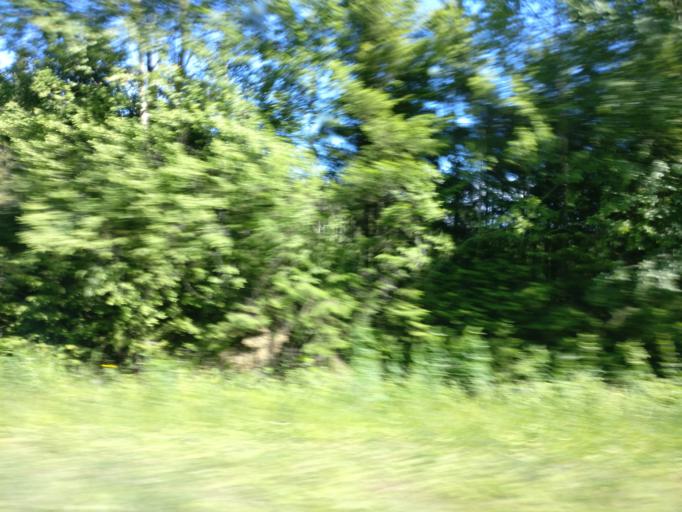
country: FI
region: Southern Savonia
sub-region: Savonlinna
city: Rantasalmi
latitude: 62.0457
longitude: 28.3210
